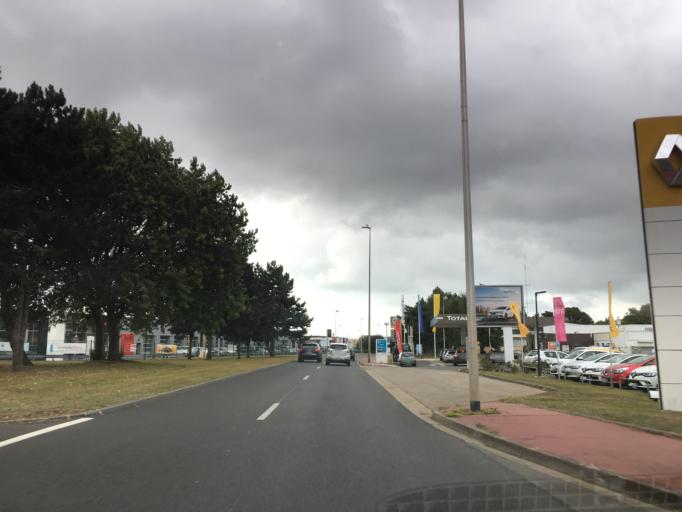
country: FR
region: Lower Normandy
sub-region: Departement du Calvados
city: Touques
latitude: 49.3531
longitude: 0.0907
